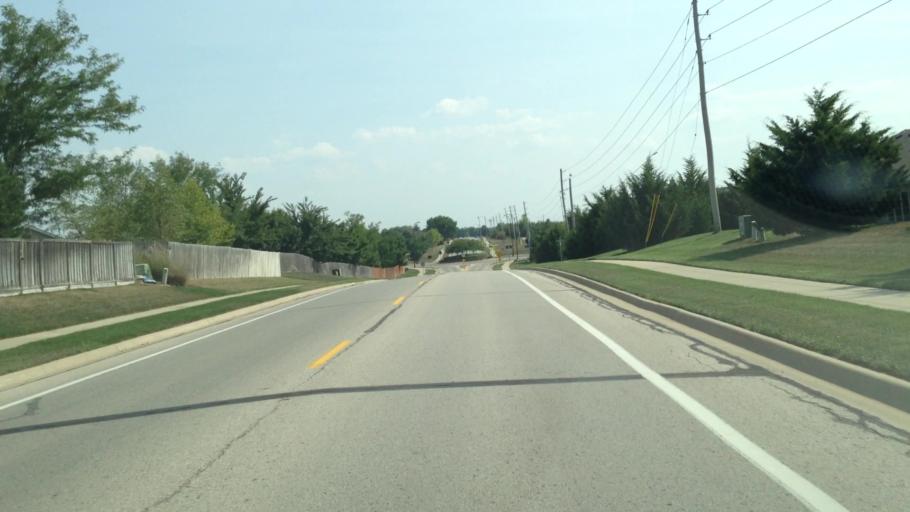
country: US
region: Kansas
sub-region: Douglas County
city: Lawrence
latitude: 38.9664
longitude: -95.3257
